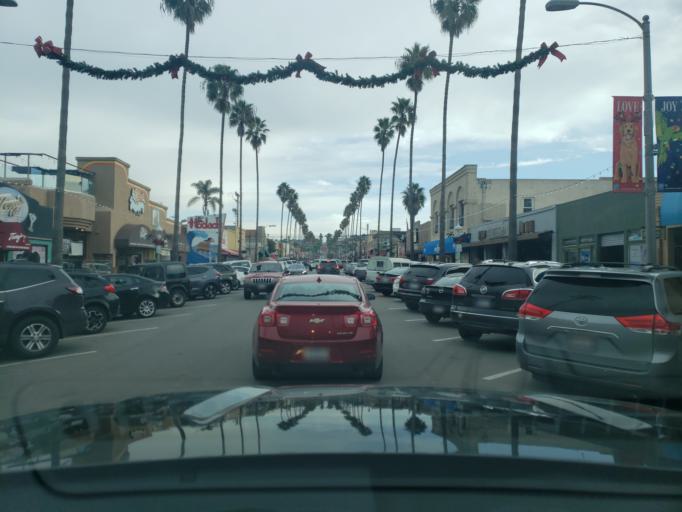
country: US
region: California
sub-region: San Diego County
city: Coronado
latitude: 32.7475
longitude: -117.2521
